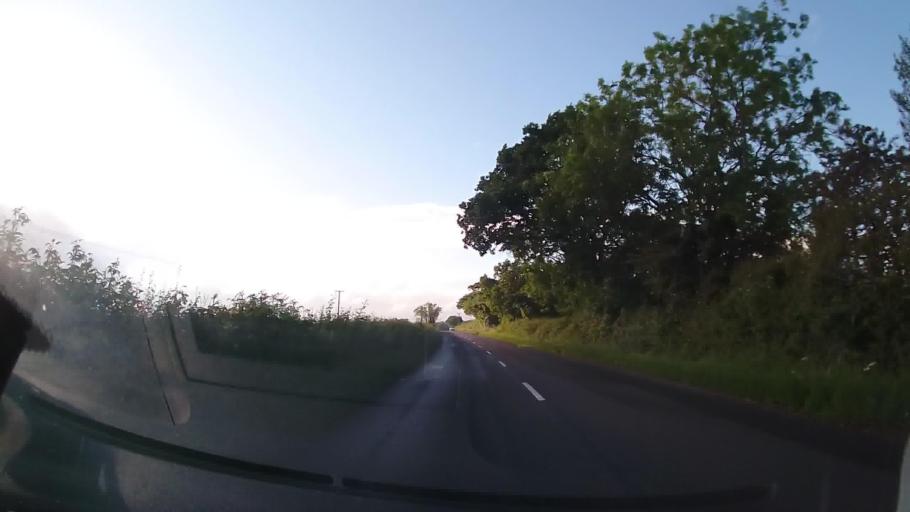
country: GB
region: England
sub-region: Leicestershire
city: Markfield
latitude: 52.6685
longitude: -1.2707
